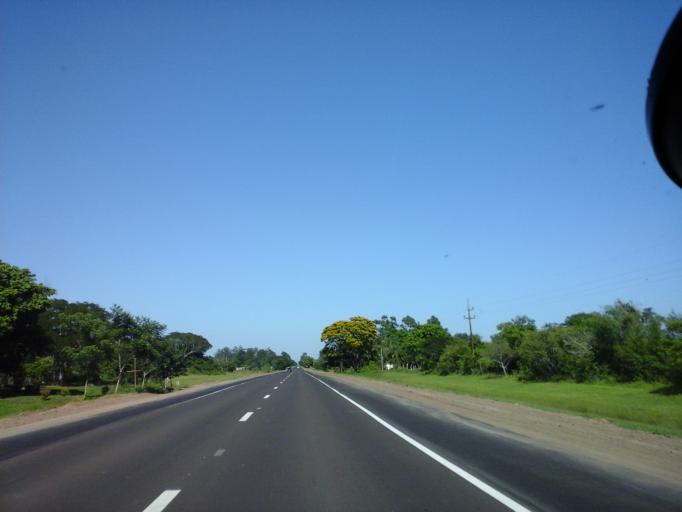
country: AR
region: Corrientes
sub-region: Departamento de Itati
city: Itati
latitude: -27.3665
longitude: -58.3253
